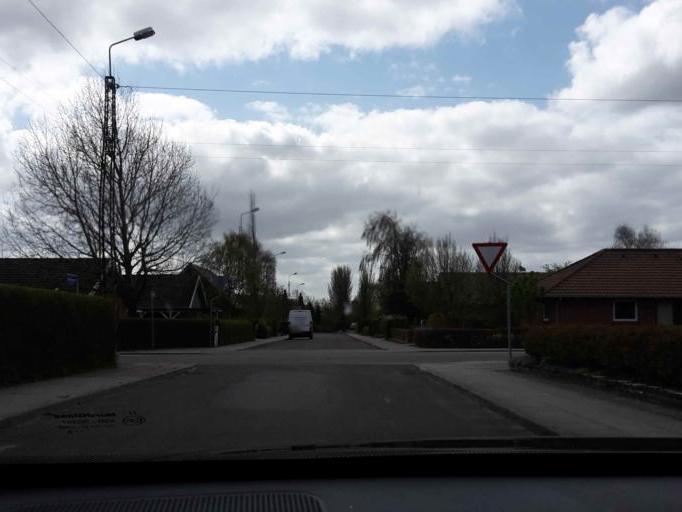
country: DK
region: South Denmark
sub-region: Varde Kommune
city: Olgod
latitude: 55.8013
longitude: 8.6192
